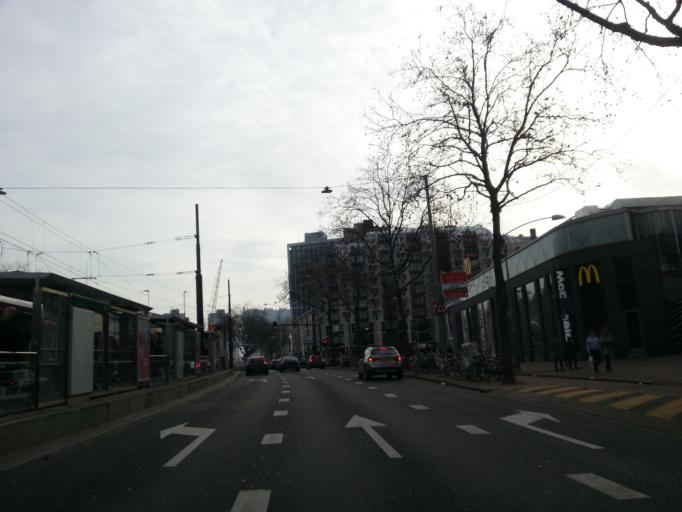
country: NL
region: South Holland
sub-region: Gemeente Rotterdam
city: Rotterdam
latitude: 51.9189
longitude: 4.4803
